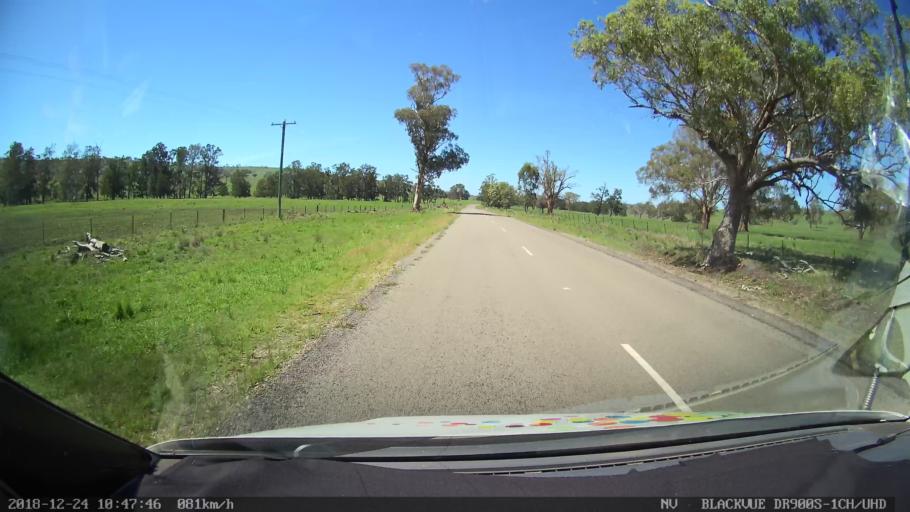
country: AU
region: New South Wales
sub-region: Upper Hunter Shire
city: Merriwa
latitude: -31.9283
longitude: 150.4298
